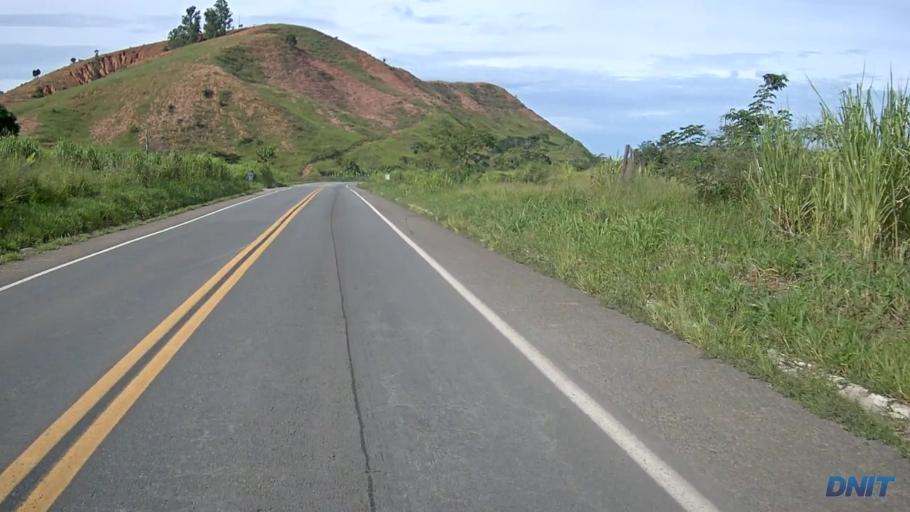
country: BR
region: Minas Gerais
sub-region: Belo Oriente
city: Belo Oriente
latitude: -19.1754
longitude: -42.2548
